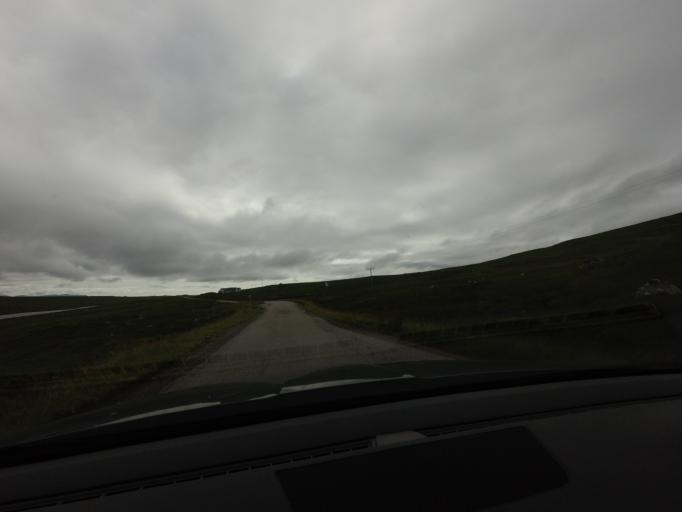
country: GB
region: Scotland
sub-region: Highland
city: Ullapool
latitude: 58.4595
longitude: -4.9195
